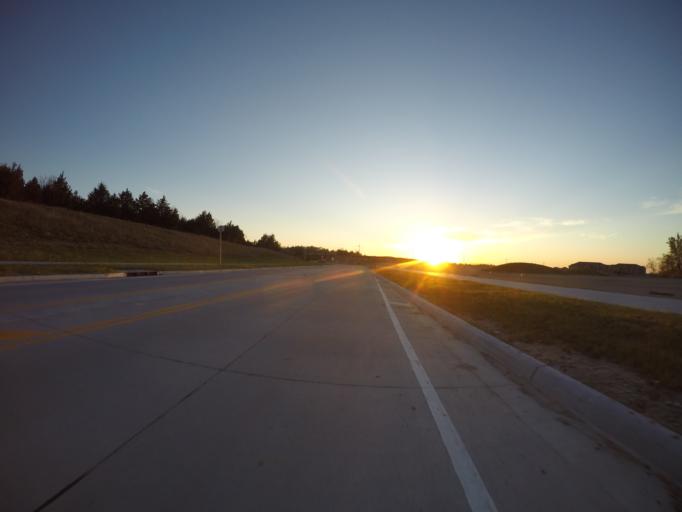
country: US
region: Kansas
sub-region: Riley County
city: Manhattan
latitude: 39.1747
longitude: -96.6441
